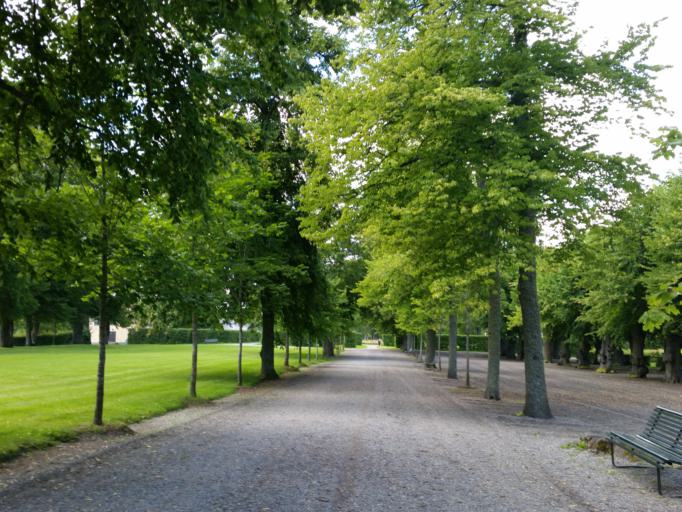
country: SE
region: Soedermanland
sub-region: Trosa Kommun
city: Trosa
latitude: 58.9509
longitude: 17.5839
